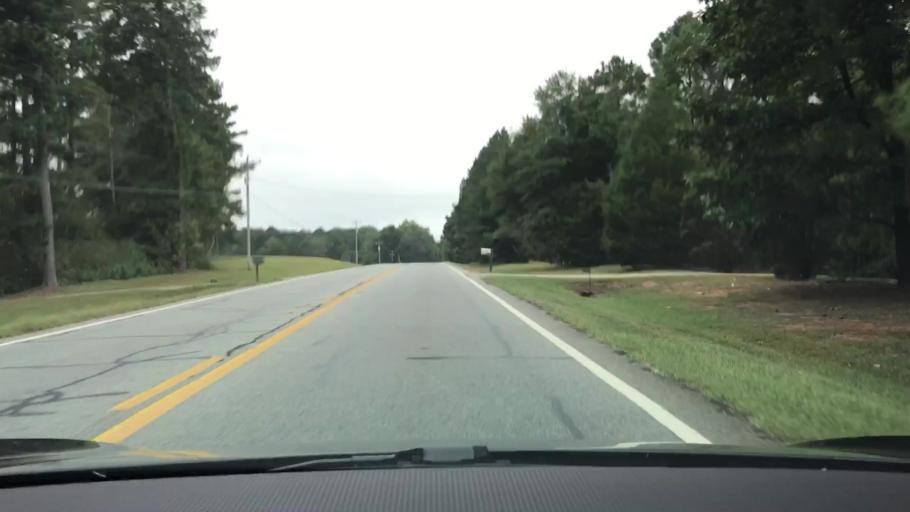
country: US
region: Georgia
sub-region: Oconee County
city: Watkinsville
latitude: 33.8081
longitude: -83.3501
